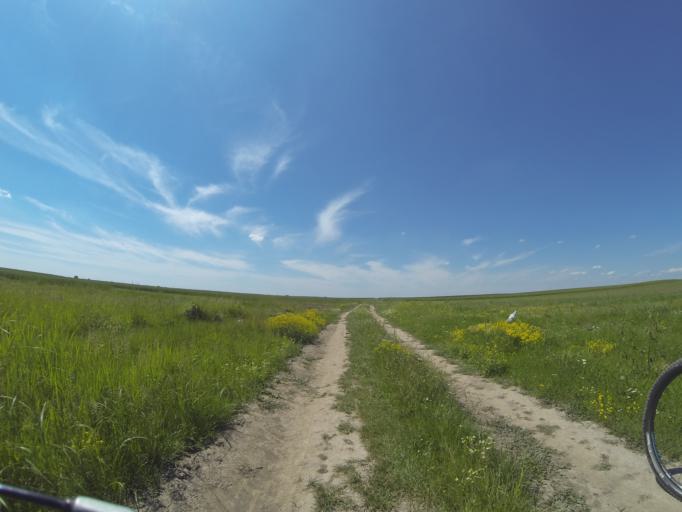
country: RO
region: Dolj
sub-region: Comuna Leu
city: Leu
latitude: 44.2162
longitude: 24.0197
